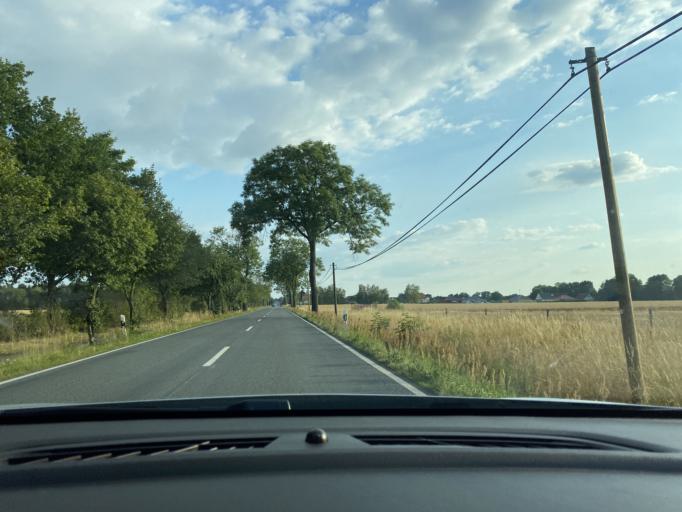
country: DE
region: Saxony
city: Konigswartha
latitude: 51.3197
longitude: 14.3354
